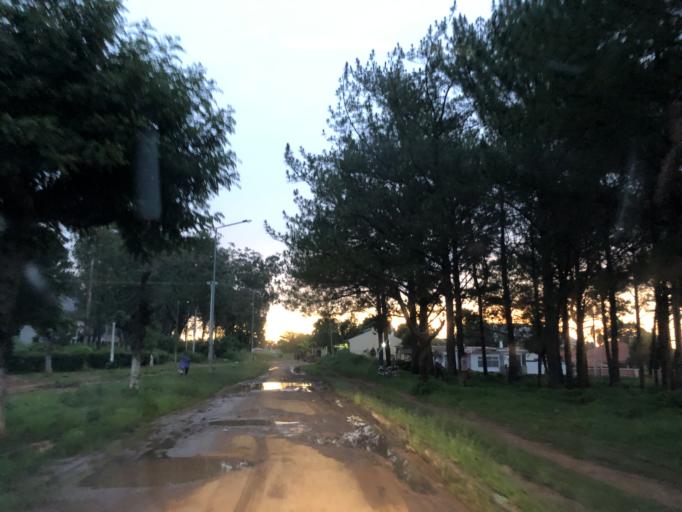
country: AO
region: Cuanza Sul
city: Uacu Cungo
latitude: -11.3664
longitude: 15.1178
